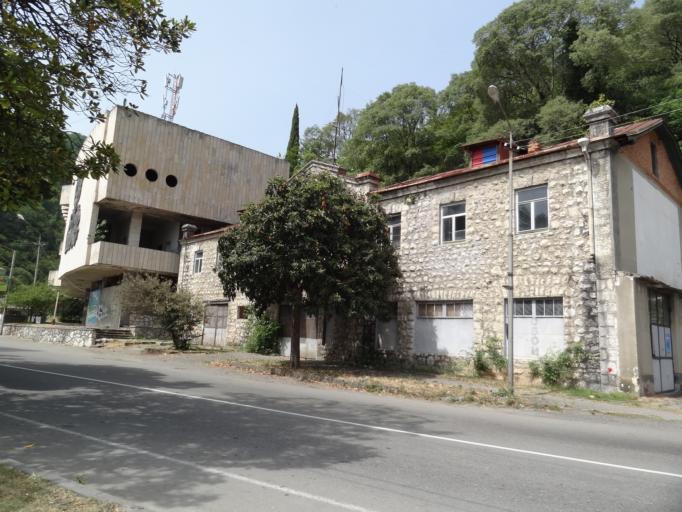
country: GE
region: Abkhazia
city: Gagra
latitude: 43.3254
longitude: 40.2245
